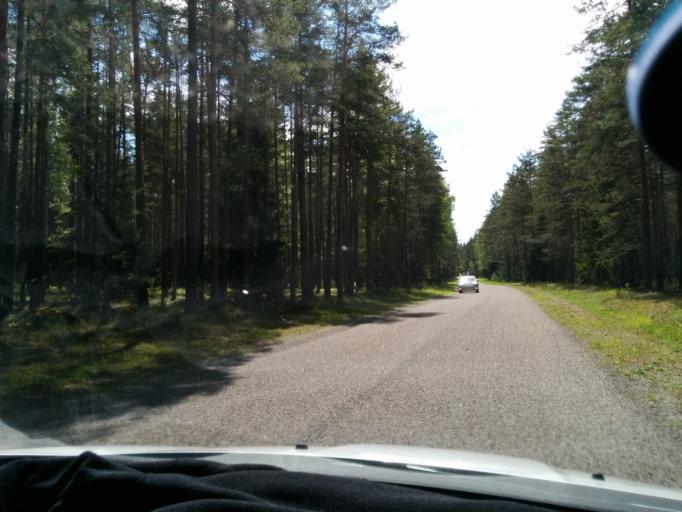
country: EE
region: Harju
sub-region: Loksa linn
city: Loksa
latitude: 59.5413
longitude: 25.9799
